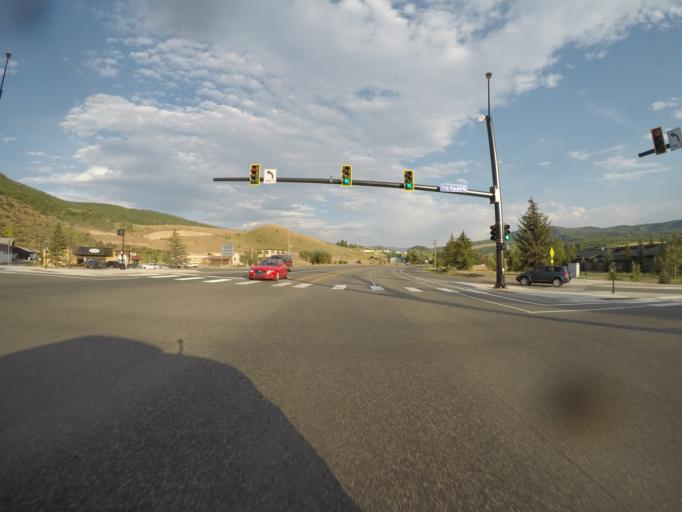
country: US
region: Colorado
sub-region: Routt County
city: Steamboat Springs
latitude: 40.5019
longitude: -106.8562
